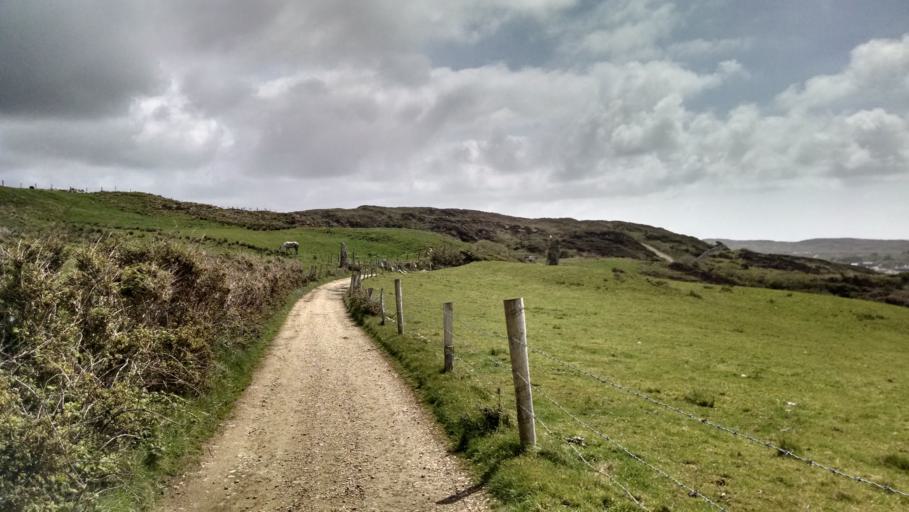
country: IE
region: Connaught
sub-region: County Galway
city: Clifden
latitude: 53.4911
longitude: -10.0533
